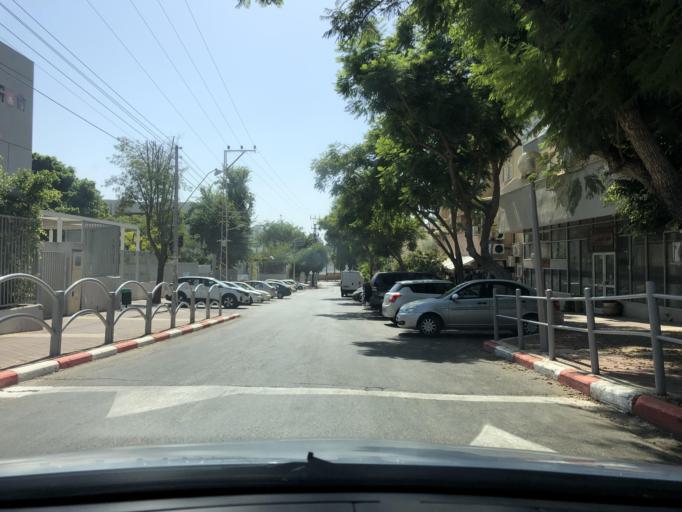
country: IL
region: Central District
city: Kfar Saba
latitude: 32.1735
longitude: 34.8963
